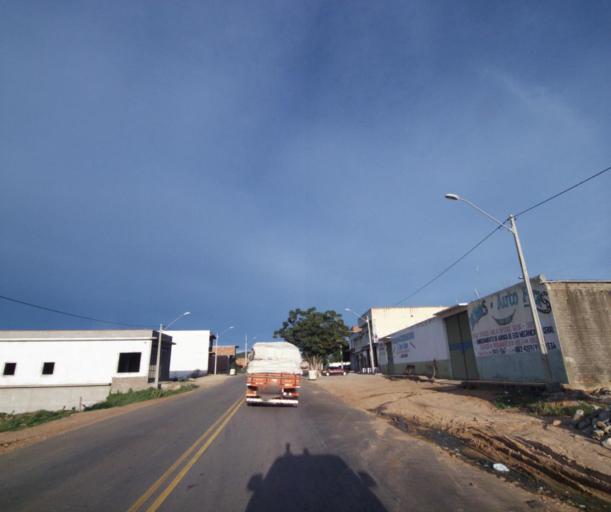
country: BR
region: Bahia
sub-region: Cacule
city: Cacule
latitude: -14.2052
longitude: -42.1199
